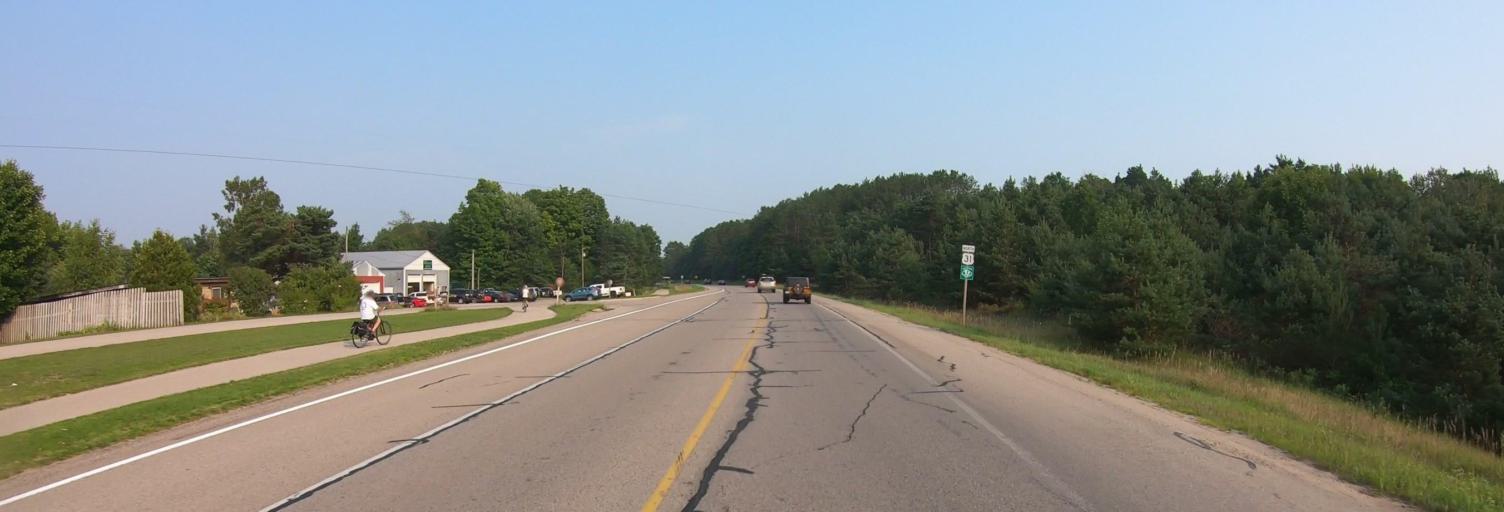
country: US
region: Michigan
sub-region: Emmet County
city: Harbor Springs
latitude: 45.3630
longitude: -85.1138
